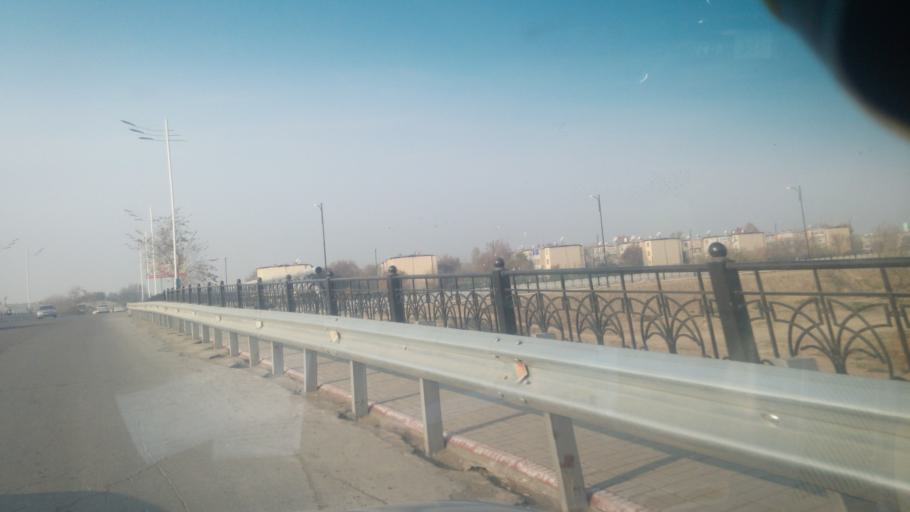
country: UZ
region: Sirdaryo
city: Guliston
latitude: 40.5117
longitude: 68.7781
